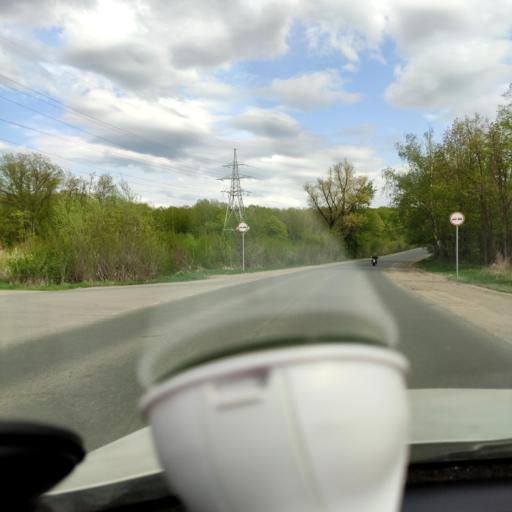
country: RU
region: Samara
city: Novosemeykino
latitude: 53.3467
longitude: 50.2416
